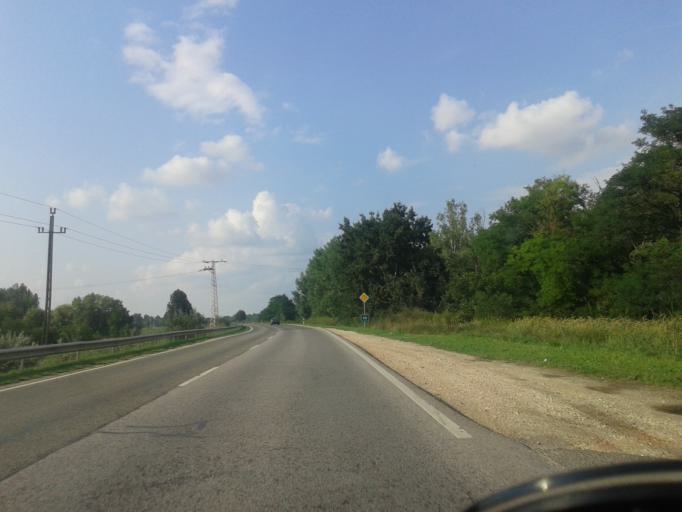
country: HU
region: Pest
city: Domsod
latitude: 47.1060
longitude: 19.0125
